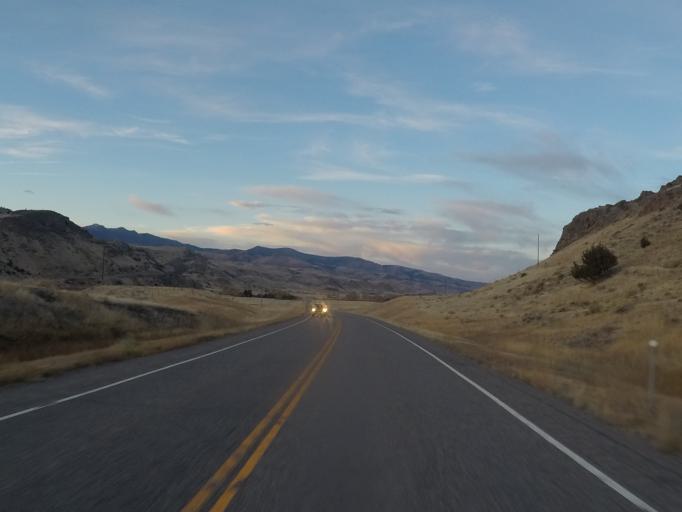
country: US
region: Montana
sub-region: Gallatin County
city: Bozeman
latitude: 45.2409
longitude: -110.8702
